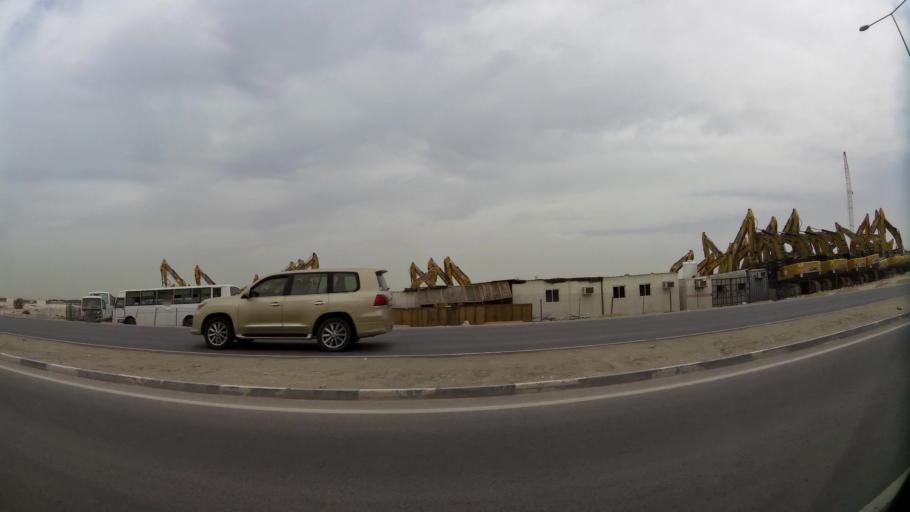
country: QA
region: Baladiyat ad Dawhah
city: Doha
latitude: 25.2314
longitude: 51.4708
